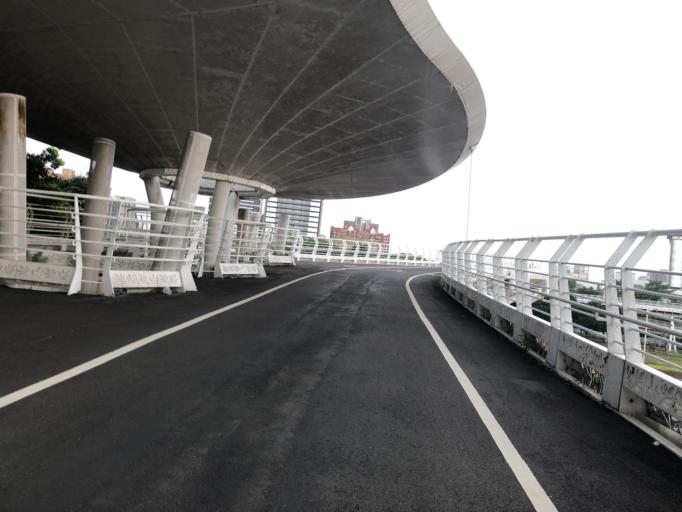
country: TW
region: Kaohsiung
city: Kaohsiung
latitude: 22.6801
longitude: 120.2984
